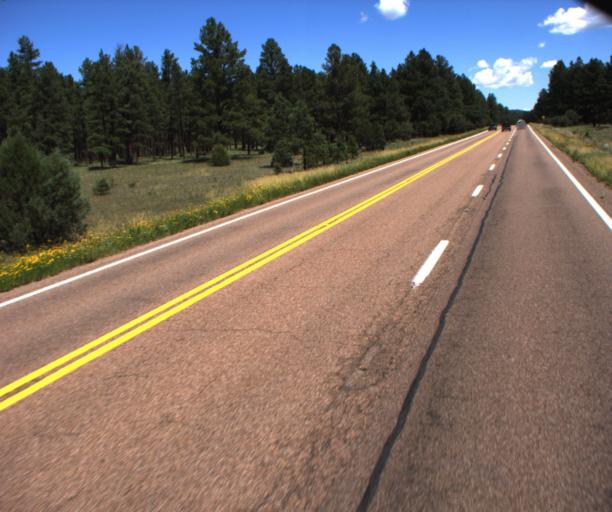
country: US
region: Arizona
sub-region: Navajo County
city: Lake of the Woods
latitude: 34.1164
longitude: -110.1357
